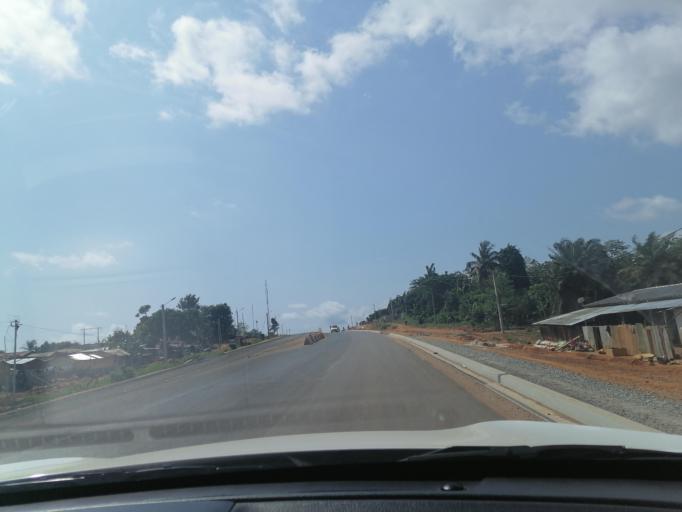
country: CI
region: Lagunes
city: Songon
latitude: 5.3217
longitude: -4.2239
